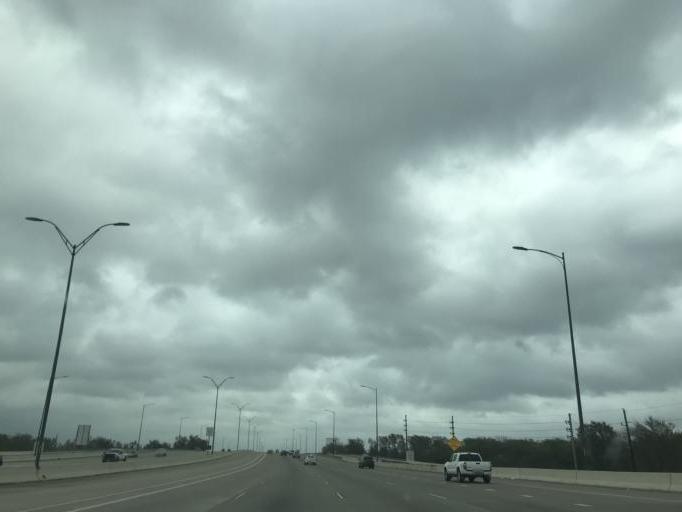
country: US
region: Texas
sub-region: Fort Bend County
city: Greatwood
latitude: 29.5660
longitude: -95.6714
